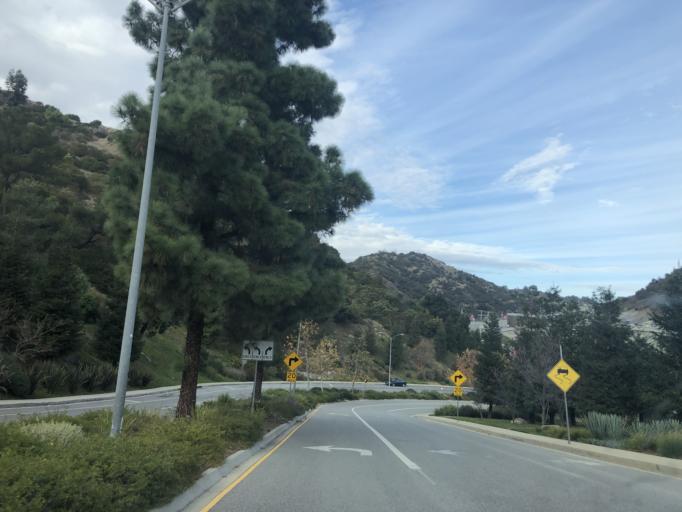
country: US
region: California
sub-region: Los Angeles County
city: Sherman Oaks
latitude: 34.1141
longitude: -118.4834
